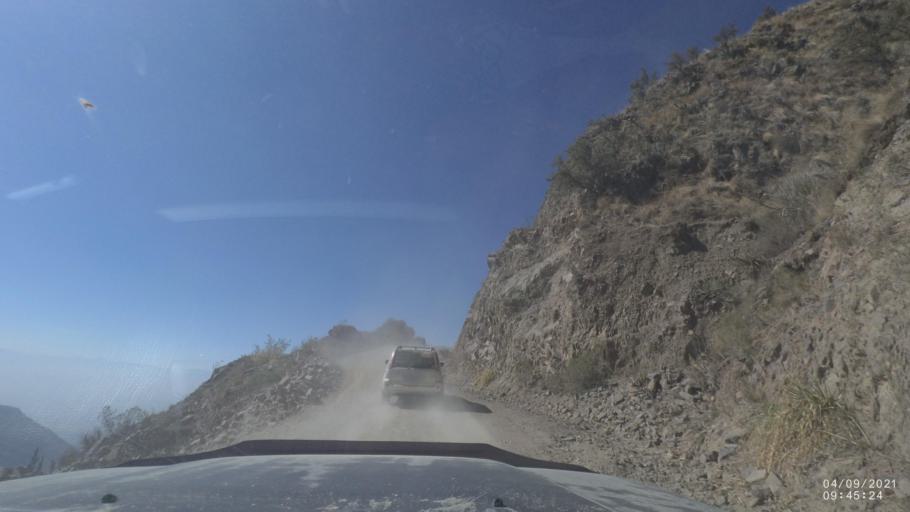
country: BO
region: Cochabamba
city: Sipe Sipe
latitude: -17.3463
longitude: -66.3901
